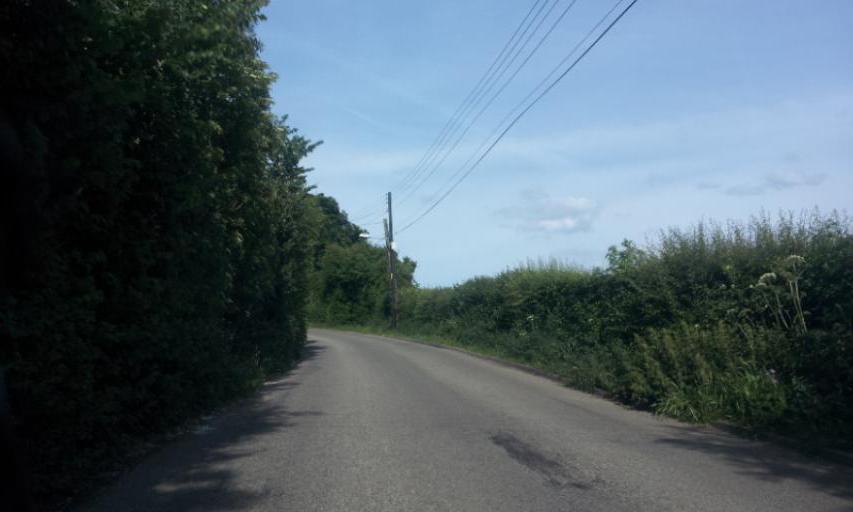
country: GB
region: England
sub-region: Kent
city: Leysdown-on-Sea
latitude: 51.4118
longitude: 0.8689
